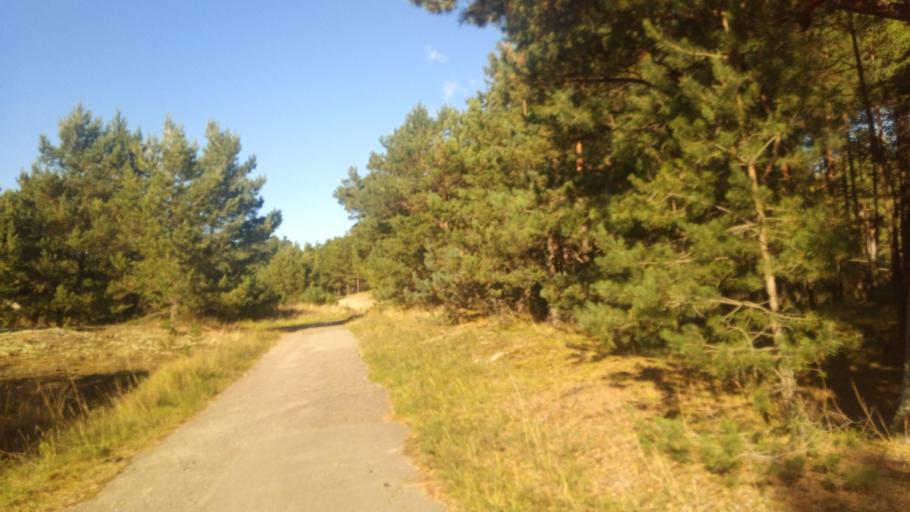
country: LT
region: Klaipedos apskritis
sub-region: Klaipeda
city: Klaipeda
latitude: 55.7126
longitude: 21.0996
